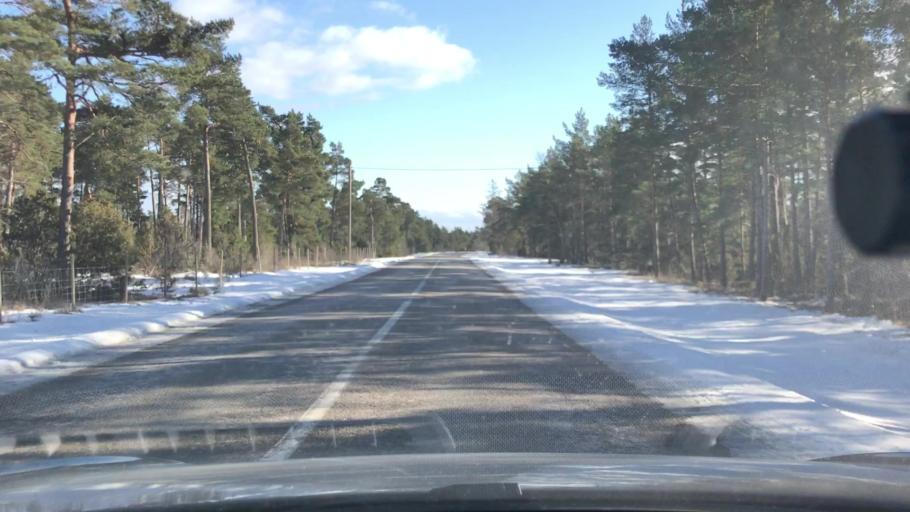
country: SE
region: Gotland
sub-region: Gotland
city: Hemse
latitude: 57.3489
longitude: 18.6896
